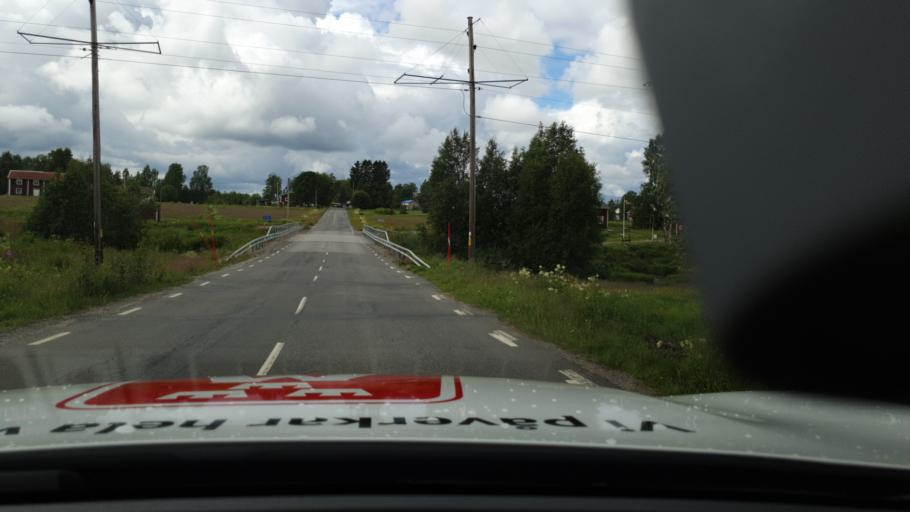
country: SE
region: Norrbotten
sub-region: Bodens Kommun
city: Saevast
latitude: 65.6070
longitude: 21.7110
